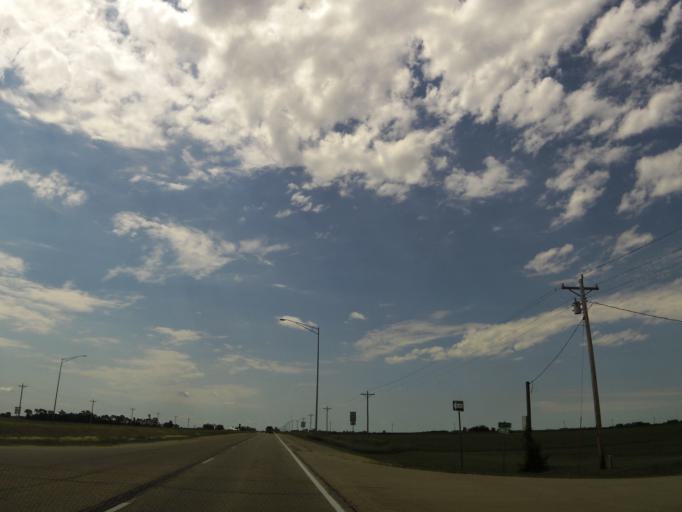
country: US
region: Iowa
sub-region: Bremer County
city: Tripoli
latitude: 42.8030
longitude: -92.3374
